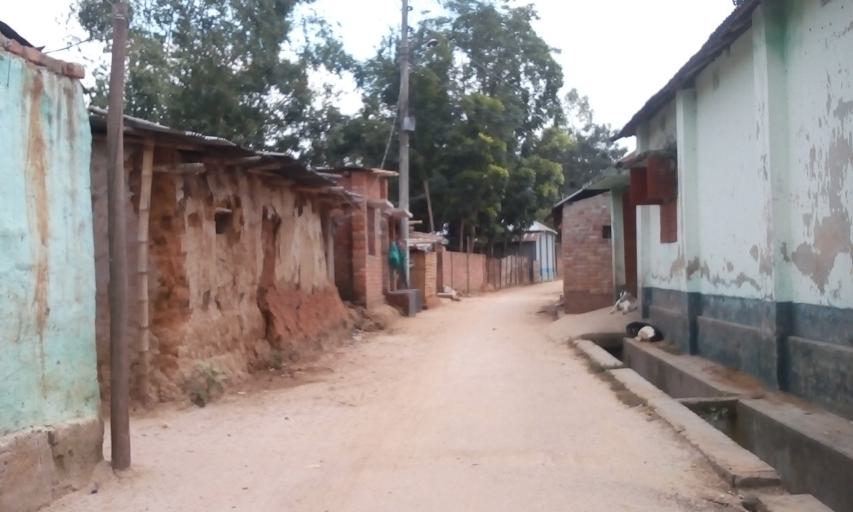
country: IN
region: West Bengal
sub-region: Dakshin Dinajpur
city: Balurghat
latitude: 25.3931
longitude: 88.9898
